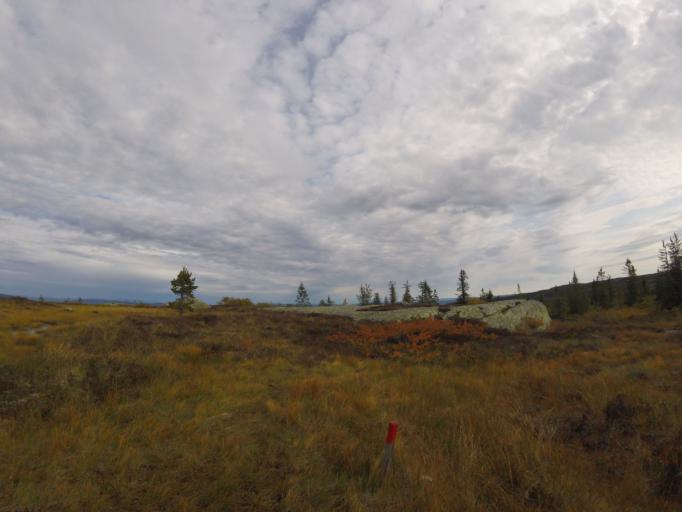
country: NO
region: Buskerud
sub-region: Rollag
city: Rollag
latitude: 59.8079
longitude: 9.3221
